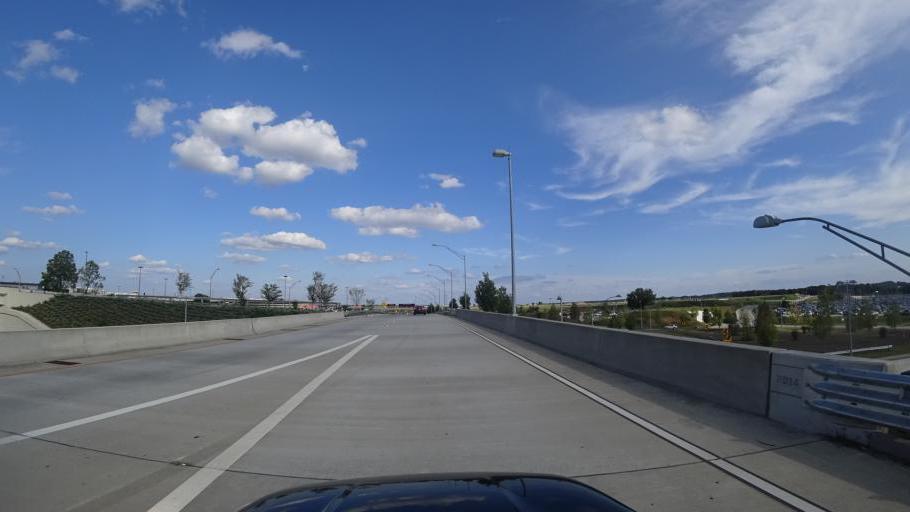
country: US
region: Georgia
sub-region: Fulton County
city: College Park
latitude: 33.6385
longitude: -84.4521
